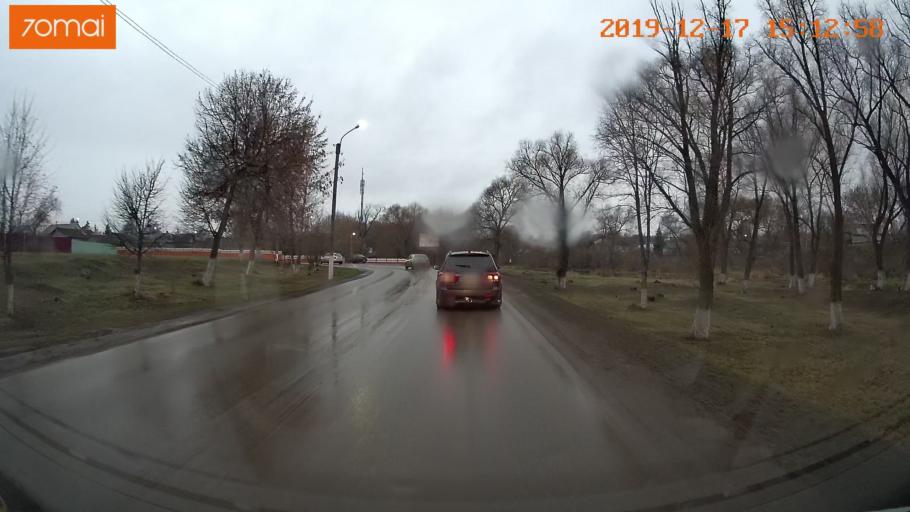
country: RU
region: Rjazan
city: Mikhaylov
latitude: 54.2345
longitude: 39.0221
